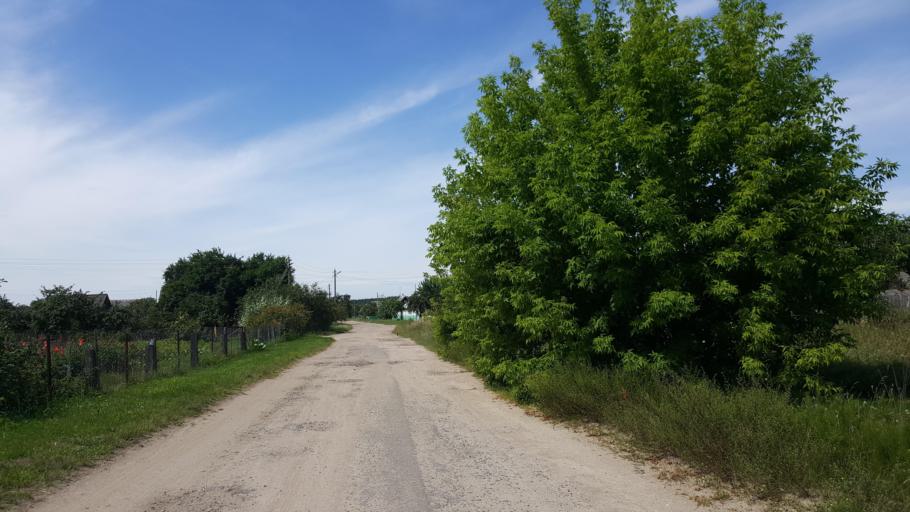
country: BY
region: Brest
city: Pruzhany
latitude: 52.5650
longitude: 24.2127
